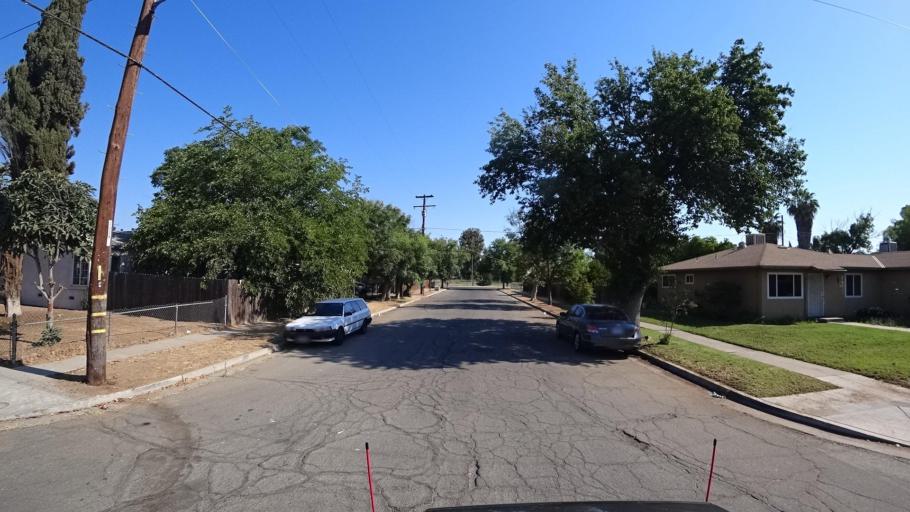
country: US
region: California
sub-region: Fresno County
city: West Park
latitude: 36.7240
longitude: -119.8244
